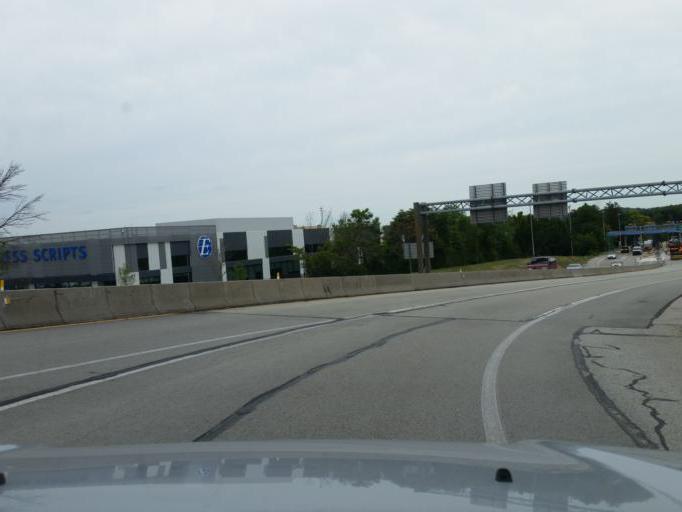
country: US
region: Pennsylvania
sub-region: Westmoreland County
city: Manor
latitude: 40.3109
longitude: -79.6791
